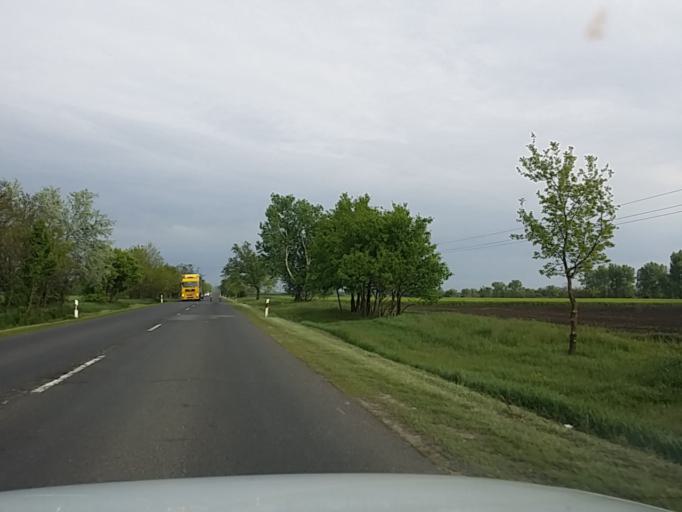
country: HU
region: Jasz-Nagykun-Szolnok
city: Jaszbereny
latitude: 47.5229
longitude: 19.8633
